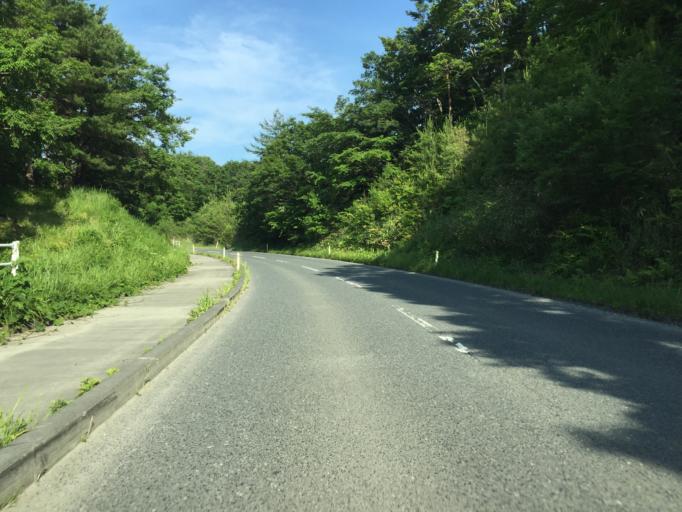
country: JP
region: Fukushima
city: Namie
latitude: 37.6666
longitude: 140.9749
